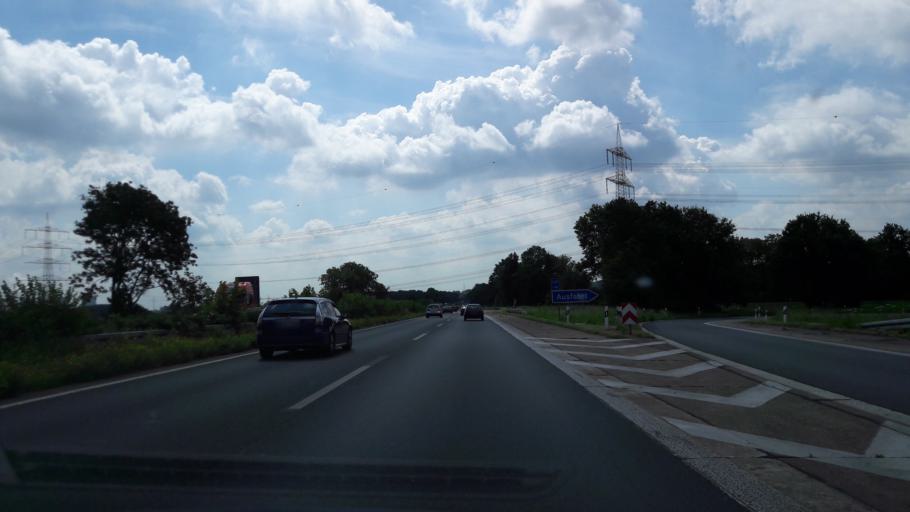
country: DE
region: North Rhine-Westphalia
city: Werne
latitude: 51.6953
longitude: 7.6677
